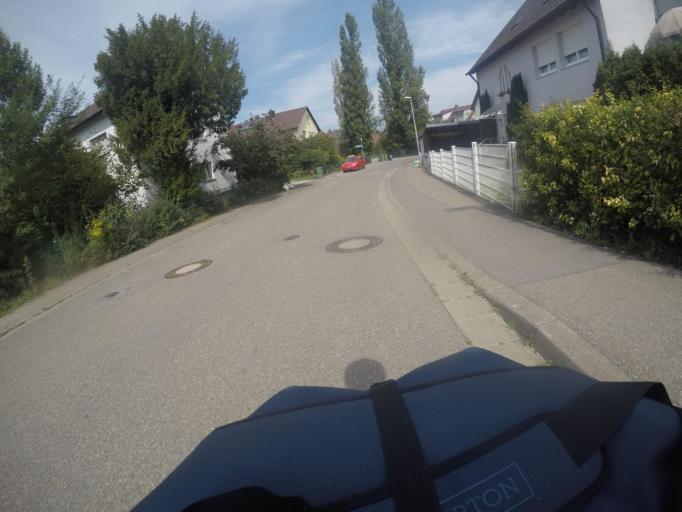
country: DE
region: Baden-Wuerttemberg
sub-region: Freiburg Region
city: Wittnau
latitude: 47.9772
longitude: 7.8037
